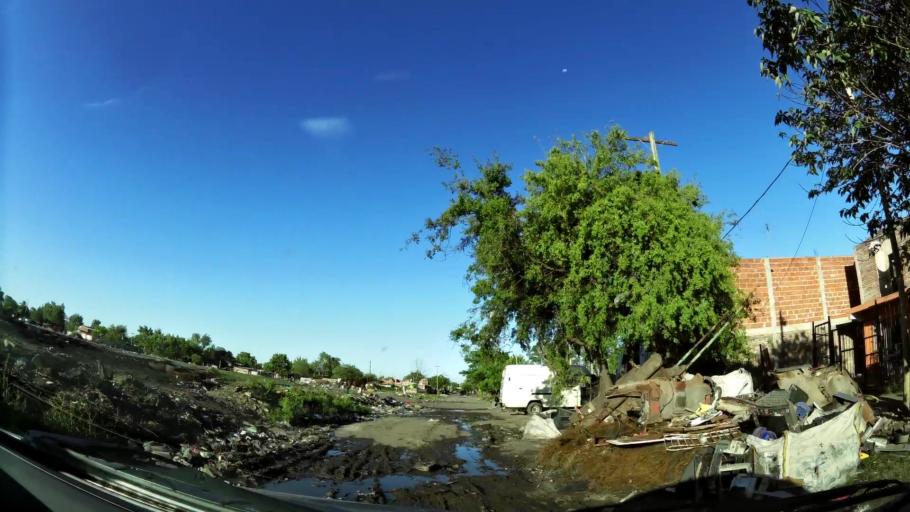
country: AR
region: Buenos Aires
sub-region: Partido de Almirante Brown
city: Adrogue
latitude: -34.7761
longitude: -58.3402
